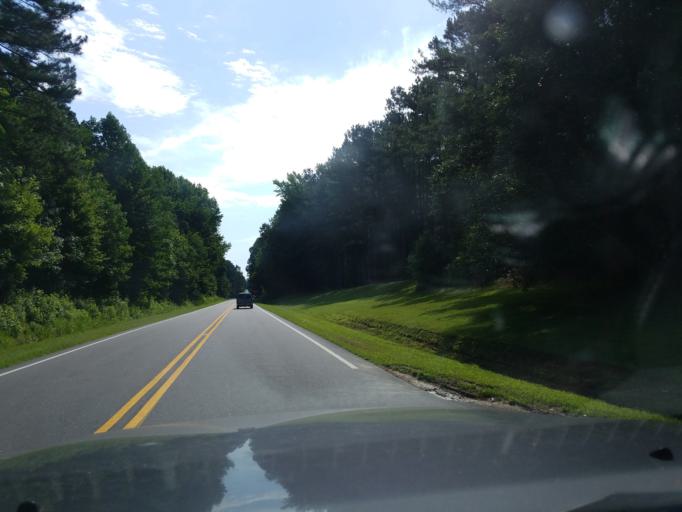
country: US
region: North Carolina
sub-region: Vance County
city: South Henderson
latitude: 36.3287
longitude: -78.4828
